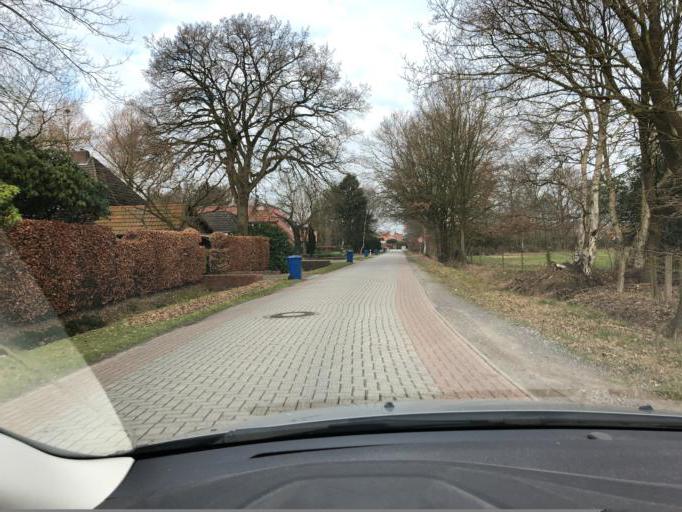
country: DE
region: Lower Saxony
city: Bad Zwischenahn
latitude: 53.1762
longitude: 8.0481
